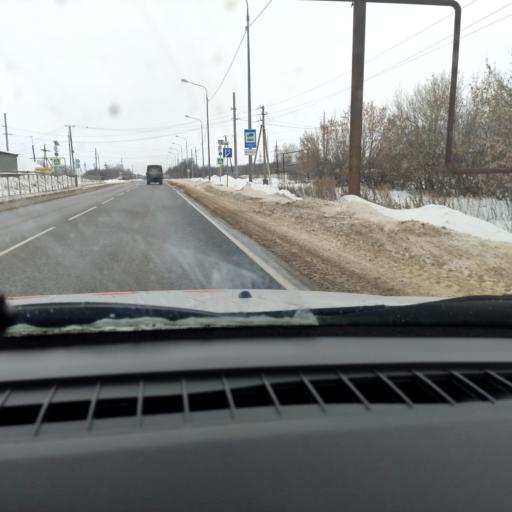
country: RU
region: Samara
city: Dubovyy Umet
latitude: 52.9620
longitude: 50.2907
